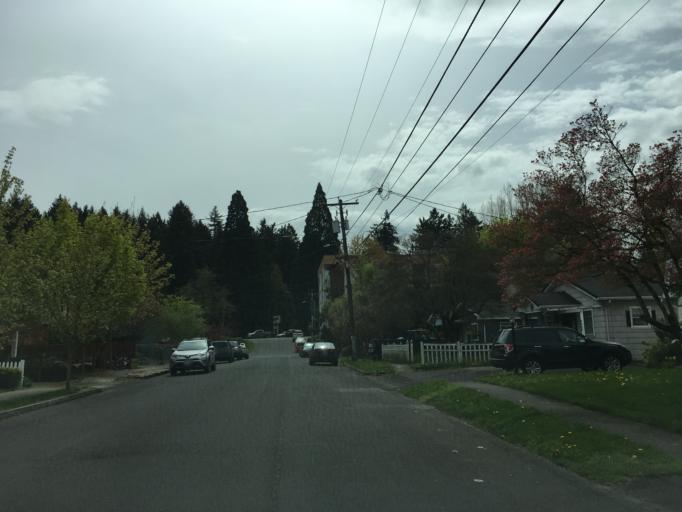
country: US
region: Oregon
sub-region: Multnomah County
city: Lents
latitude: 45.5549
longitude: -122.5757
